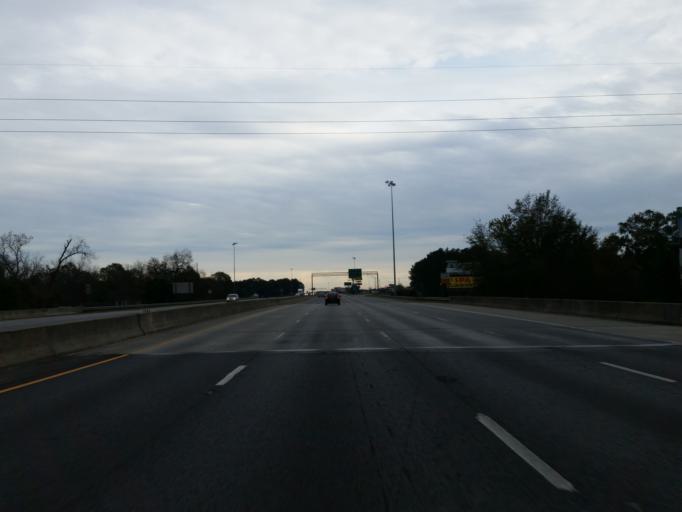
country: US
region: Georgia
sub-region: Tift County
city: Unionville
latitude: 31.4351
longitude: -83.5213
